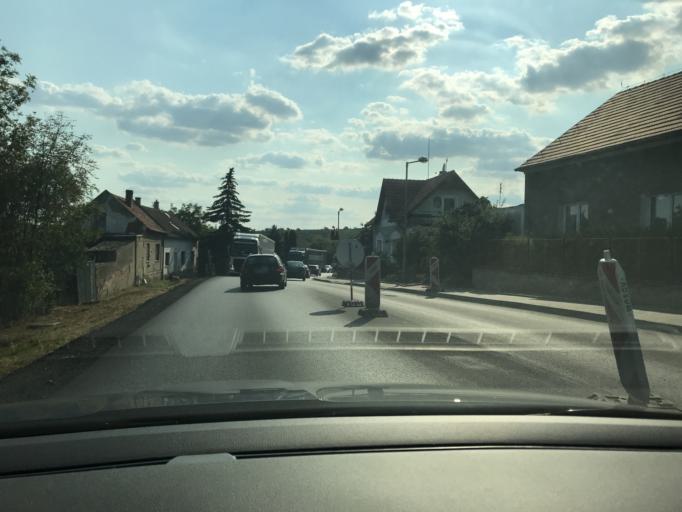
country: CZ
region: Central Bohemia
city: Pchery
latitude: 50.2474
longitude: 14.1443
